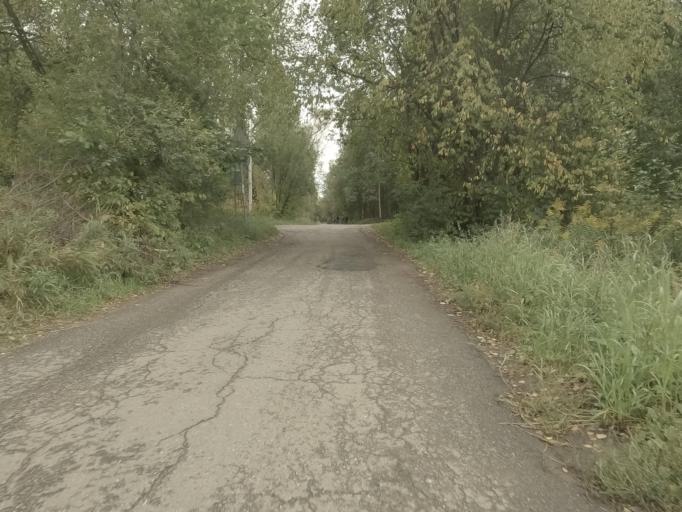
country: RU
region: St.-Petersburg
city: Krasnogvargeisky
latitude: 59.9731
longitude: 30.5136
